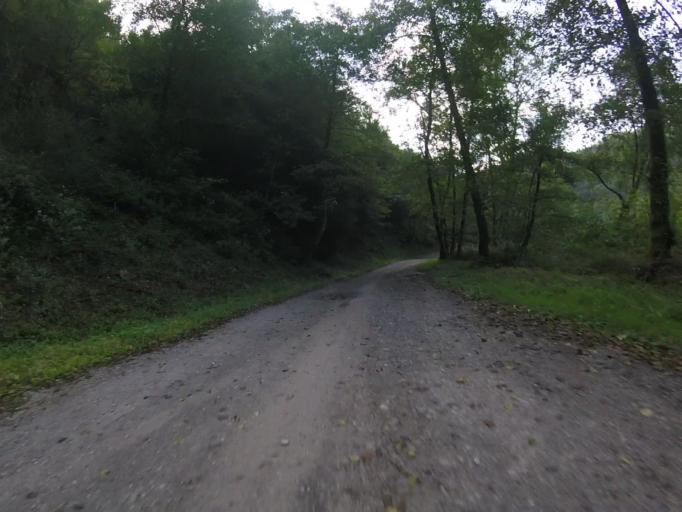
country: ES
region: Basque Country
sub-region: Provincia de Guipuzcoa
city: Elduayen
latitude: 43.1749
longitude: -1.9783
